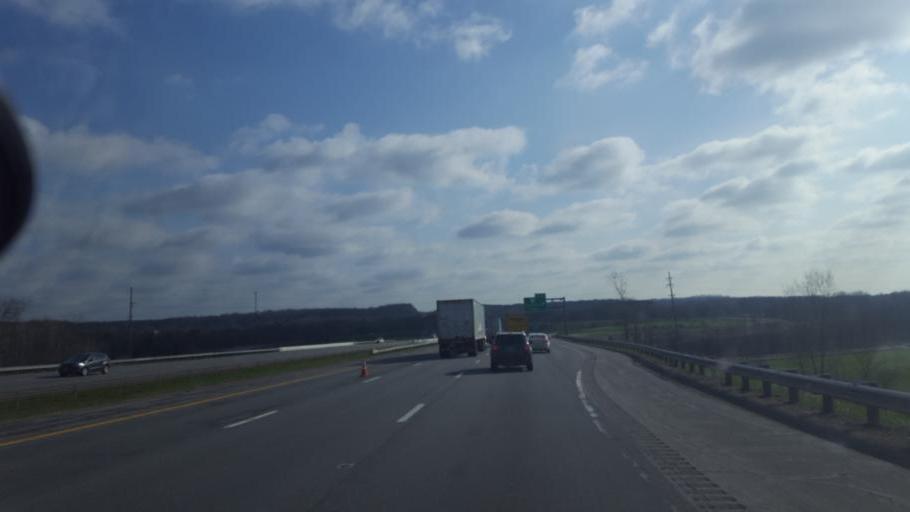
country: US
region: Ohio
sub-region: Richland County
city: Lincoln Heights
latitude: 40.7345
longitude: -82.4652
